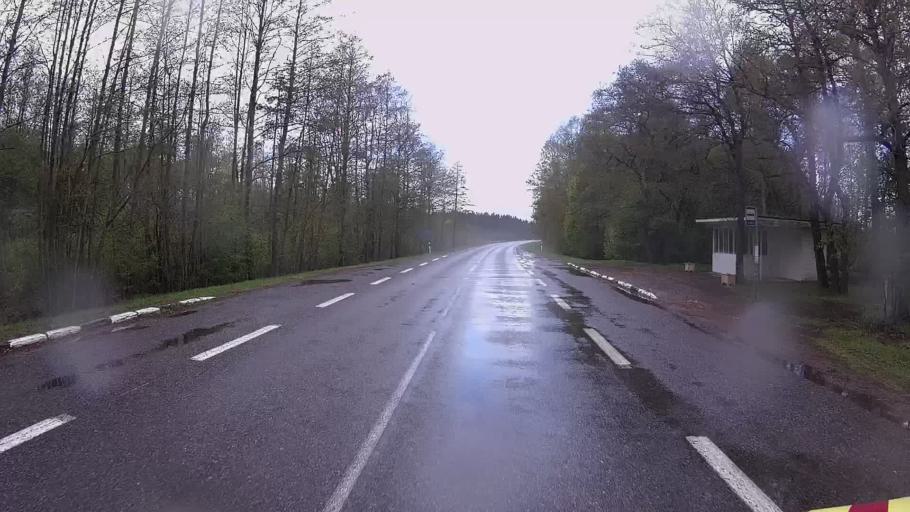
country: EE
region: Hiiumaa
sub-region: Kaerdla linn
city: Kardla
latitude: 58.8324
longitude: 22.8219
